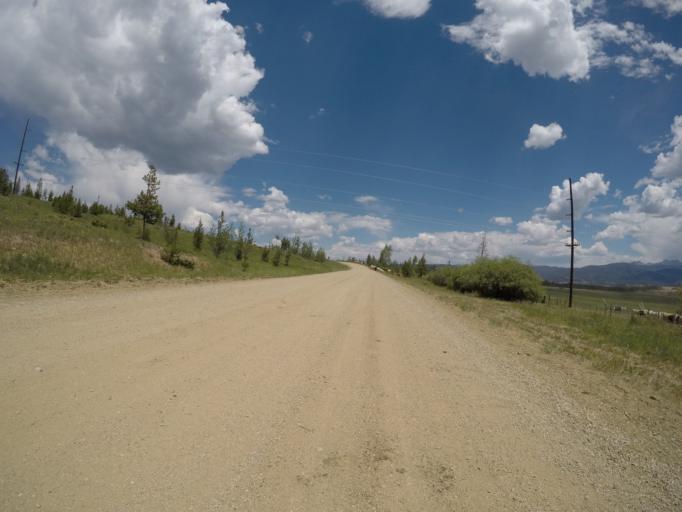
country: US
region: Colorado
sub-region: Grand County
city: Fraser
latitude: 39.9586
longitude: -105.8692
